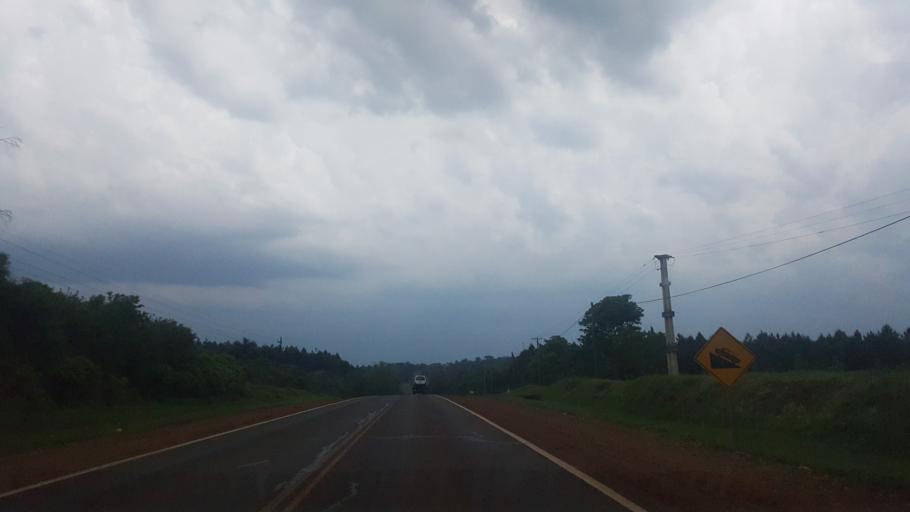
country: AR
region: Misiones
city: Santo Pipo
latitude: -27.1355
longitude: -55.3968
